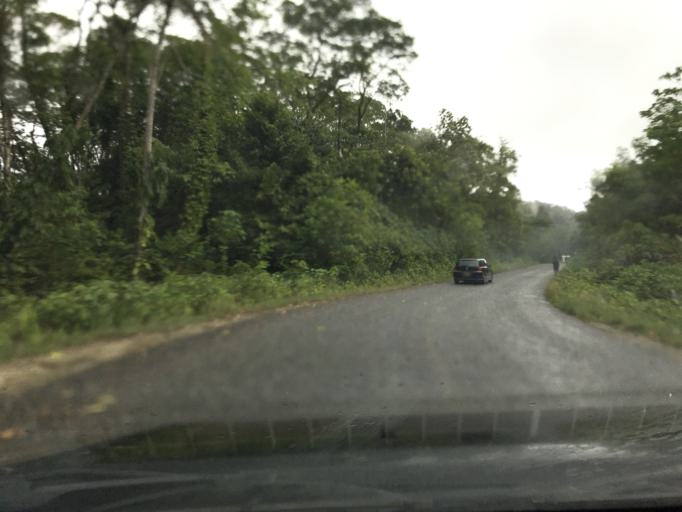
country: SB
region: Western Province
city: Gizo
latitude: -8.3155
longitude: 157.2535
